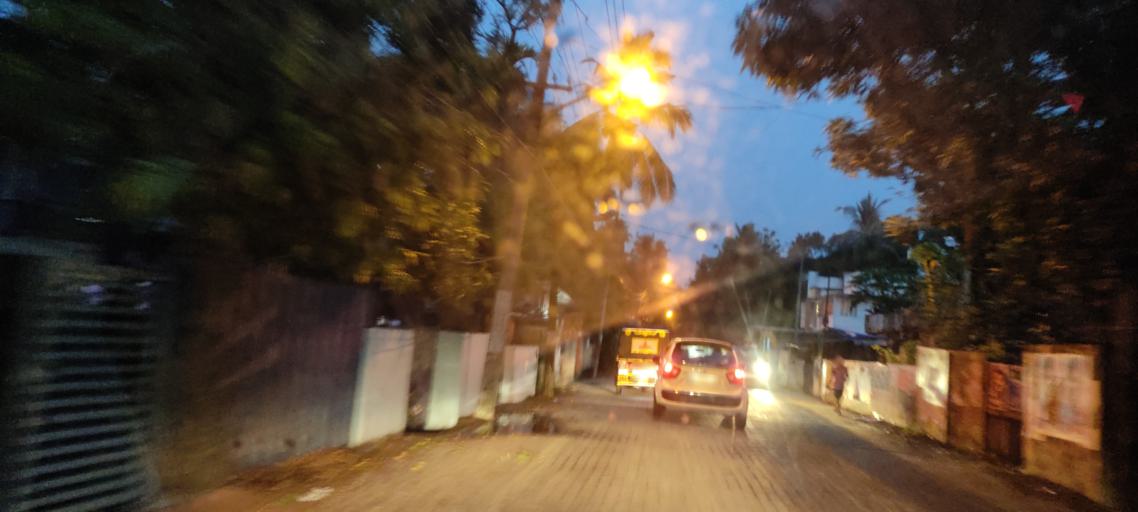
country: IN
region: Kerala
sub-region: Ernakulam
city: Cochin
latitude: 9.9003
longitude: 76.2953
